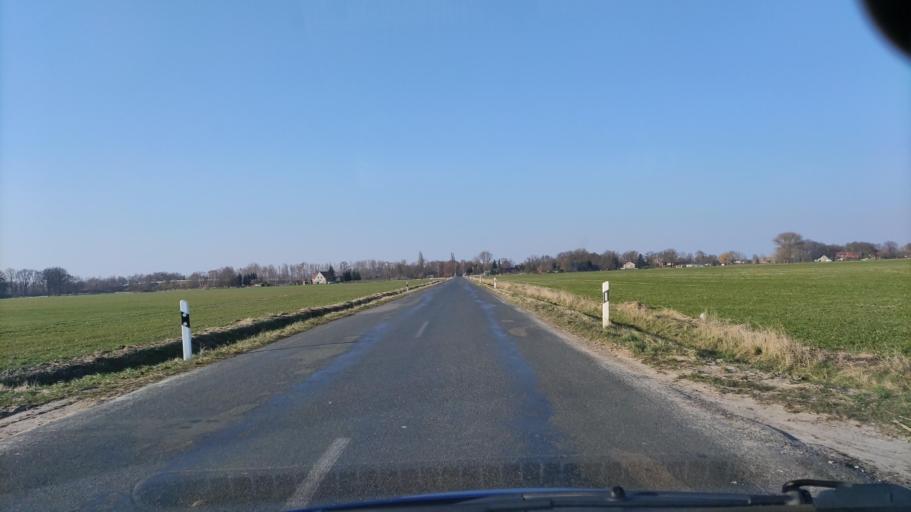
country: DE
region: Brandenburg
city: Wittenberge
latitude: 52.9620
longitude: 11.7473
